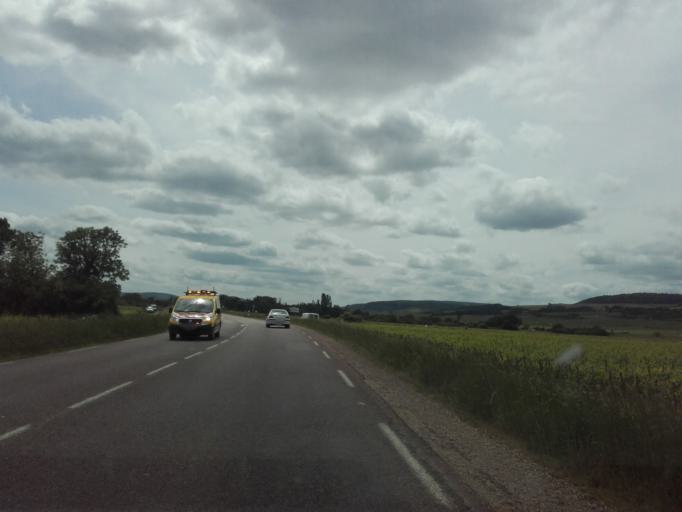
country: FR
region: Bourgogne
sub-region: Departement de la Cote-d'Or
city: Meursault
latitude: 46.9690
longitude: 4.7772
